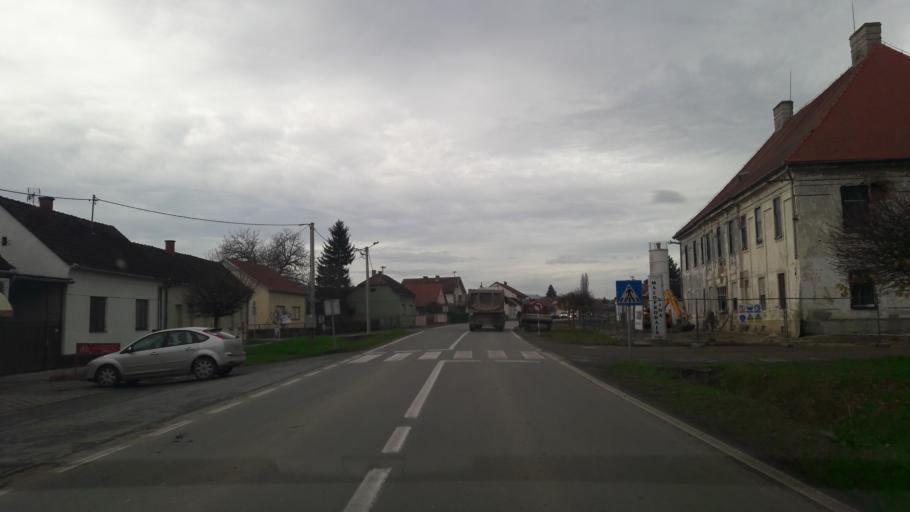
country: HR
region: Osjecko-Baranjska
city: Fericanci
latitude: 45.5238
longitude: 17.9745
